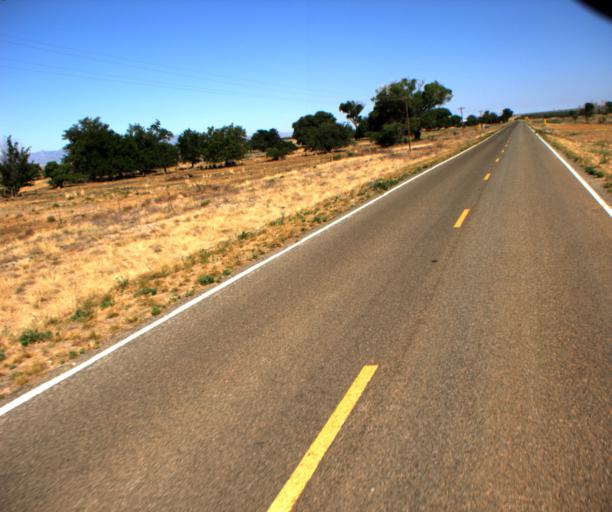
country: US
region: Arizona
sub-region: Graham County
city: Swift Trail Junction
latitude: 32.5858
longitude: -109.9633
